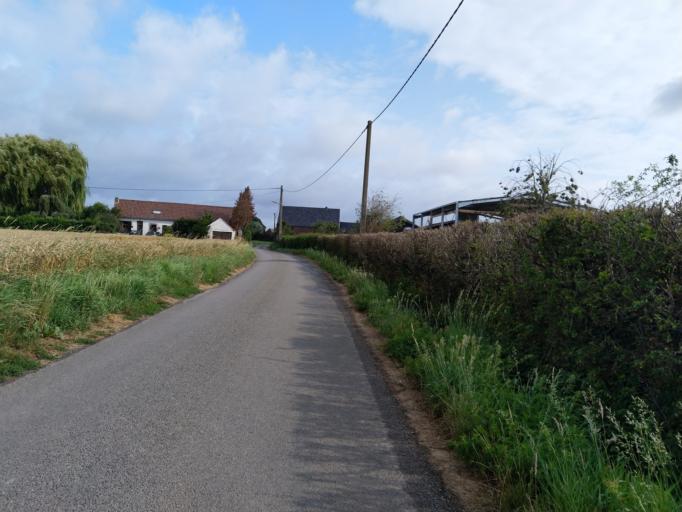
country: BE
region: Wallonia
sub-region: Province du Hainaut
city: Lens
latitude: 50.5396
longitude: 3.8817
